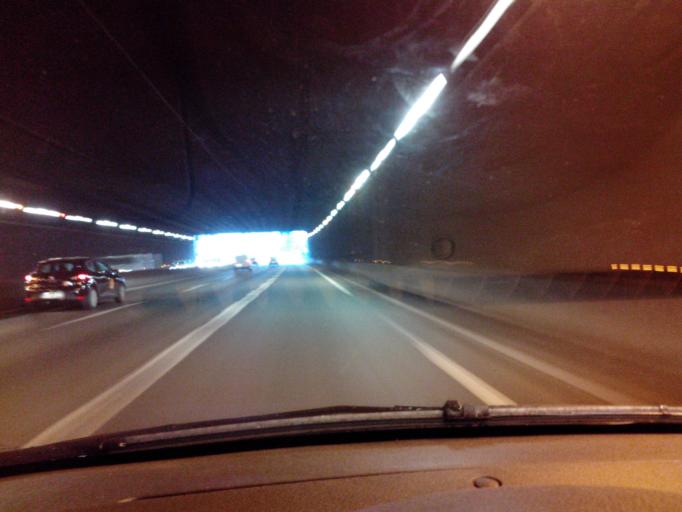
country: FR
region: Ile-de-France
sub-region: Departement du Val-de-Marne
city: Fresnes
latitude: 48.7586
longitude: 2.3257
